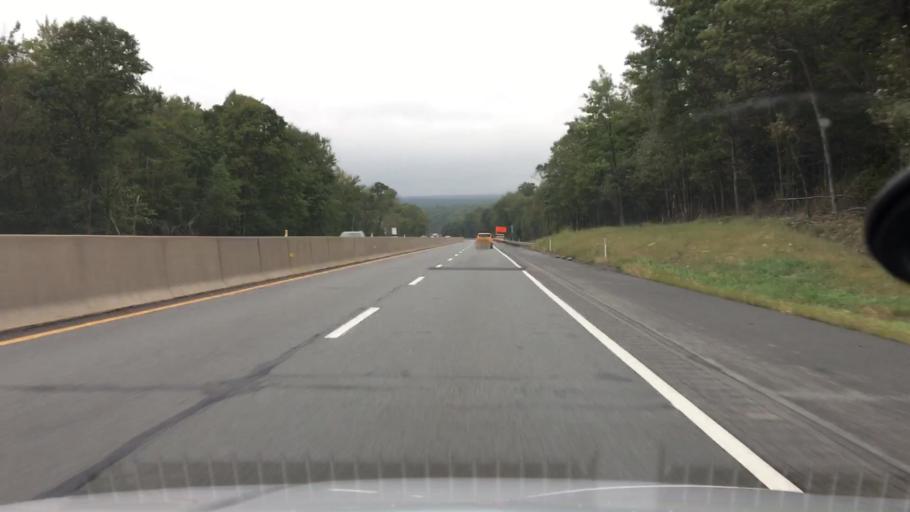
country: US
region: Pennsylvania
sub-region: Luzerne County
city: White Haven
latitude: 41.0922
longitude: -75.7407
